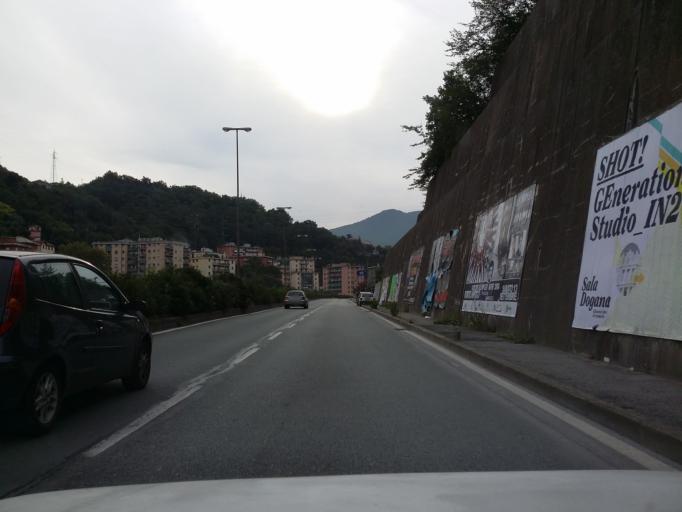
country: IT
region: Liguria
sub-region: Provincia di Genova
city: Piccarello
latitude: 44.4535
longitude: 8.9874
